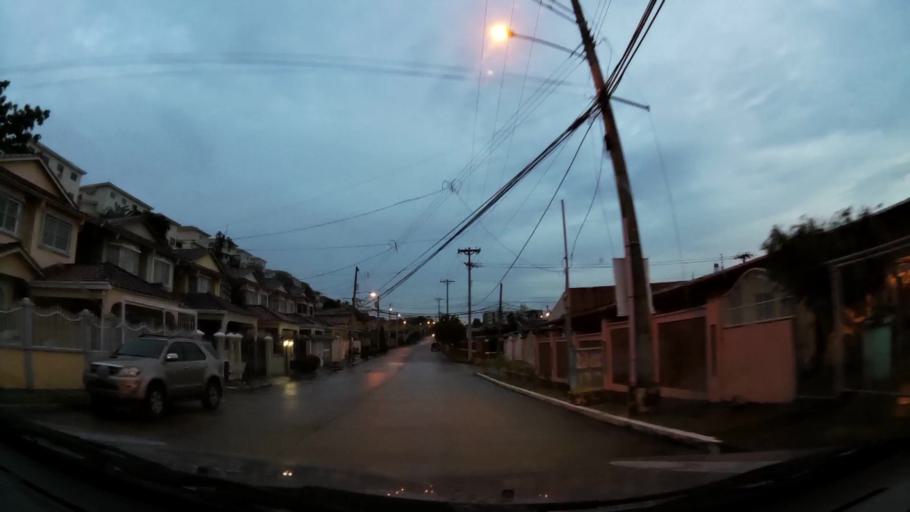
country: PA
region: Panama
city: Las Cumbres
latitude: 9.0443
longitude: -79.5226
